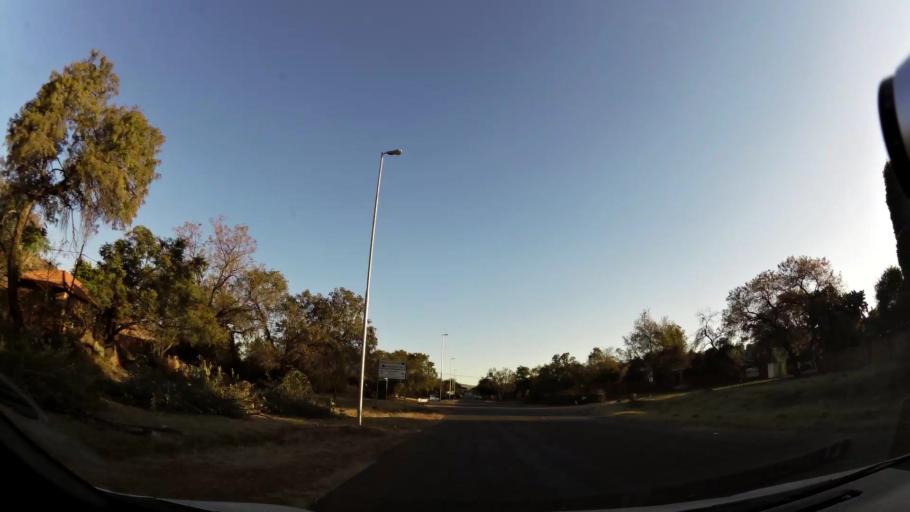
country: ZA
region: North-West
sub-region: Bojanala Platinum District Municipality
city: Rustenburg
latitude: -25.7160
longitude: 27.2387
